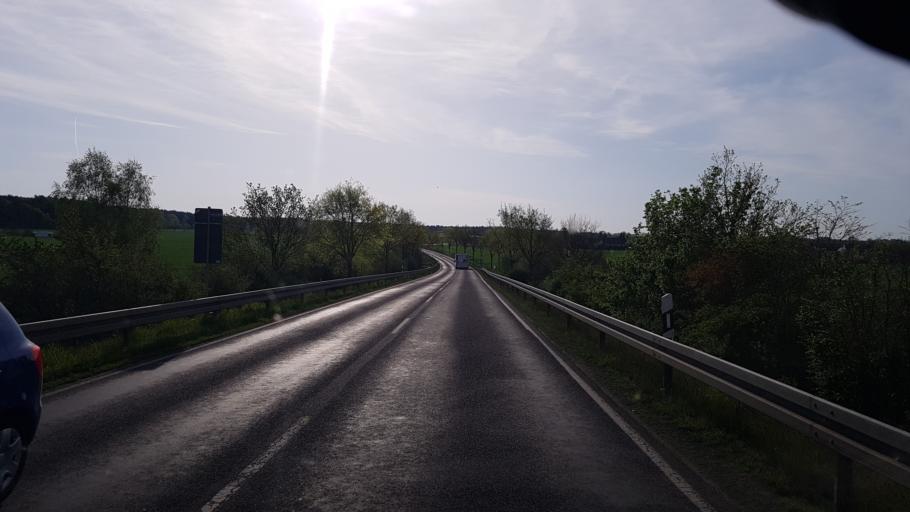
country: DE
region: Brandenburg
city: Ortrand
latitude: 51.3842
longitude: 13.7517
